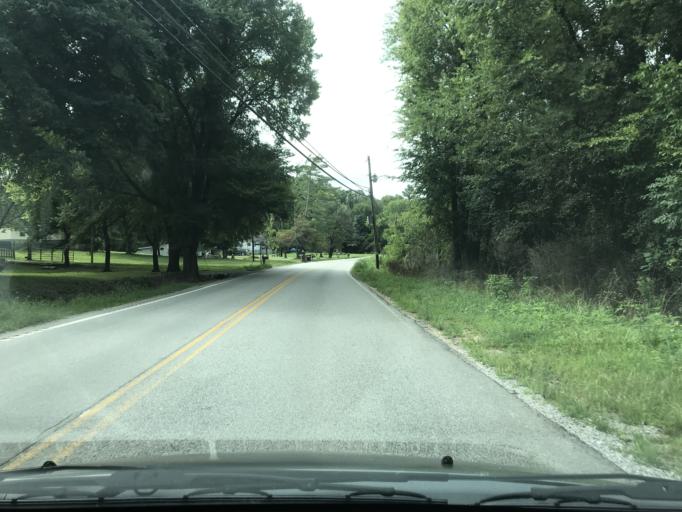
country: US
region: Tennessee
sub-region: Hamilton County
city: Lakesite
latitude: 35.1873
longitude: -85.0669
